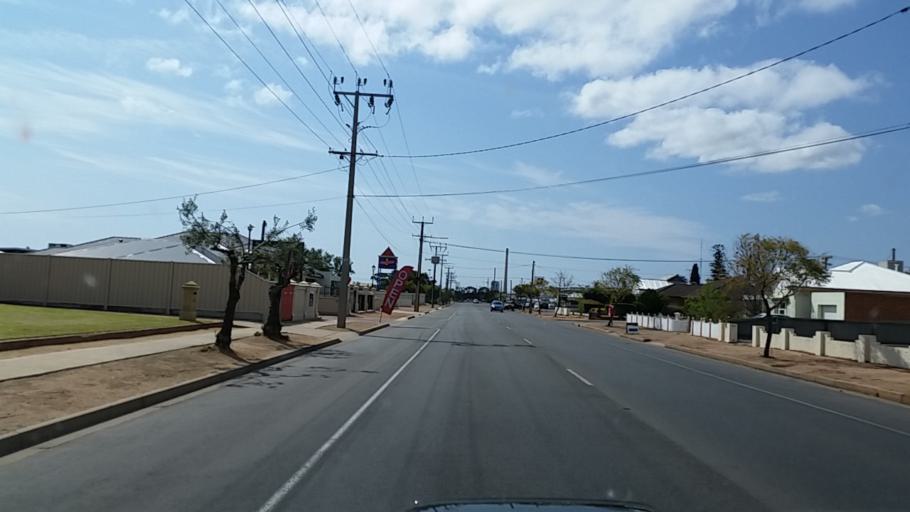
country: AU
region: South Australia
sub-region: Port Pirie City and Dists
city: Port Pirie
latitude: -33.1960
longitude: 138.0102
